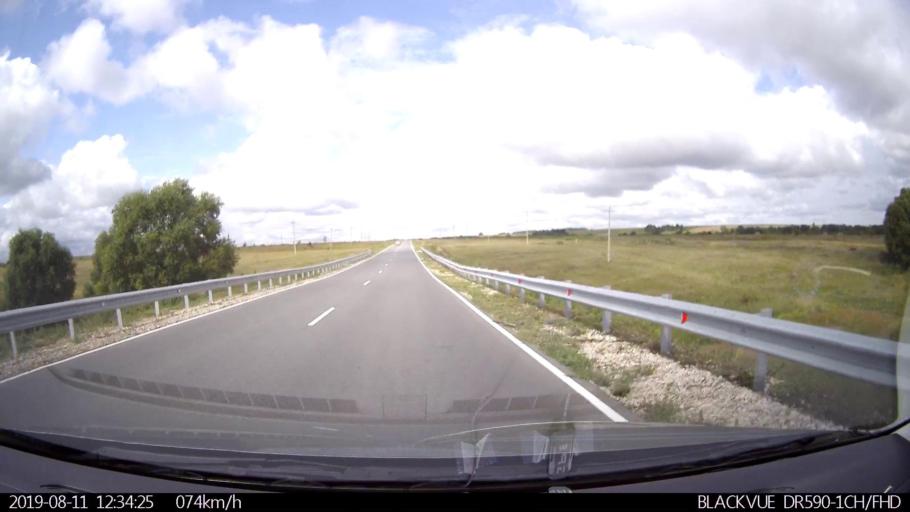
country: RU
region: Ulyanovsk
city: Ignatovka
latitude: 53.8167
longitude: 47.8431
